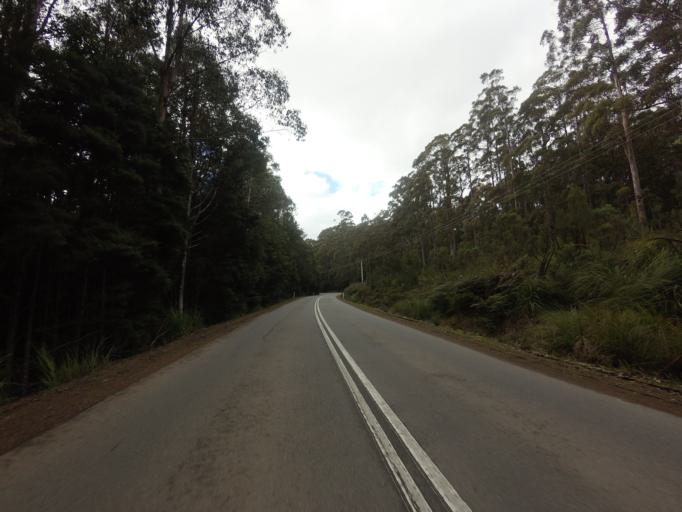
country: AU
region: Tasmania
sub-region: Huon Valley
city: Geeveston
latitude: -43.3747
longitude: 146.9557
